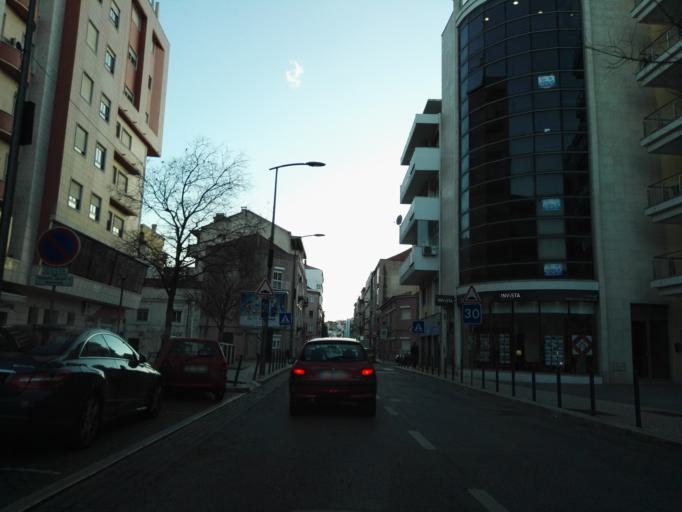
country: PT
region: Lisbon
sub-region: Vila Franca de Xira
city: Vila Franca de Xira
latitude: 38.9574
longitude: -8.9870
